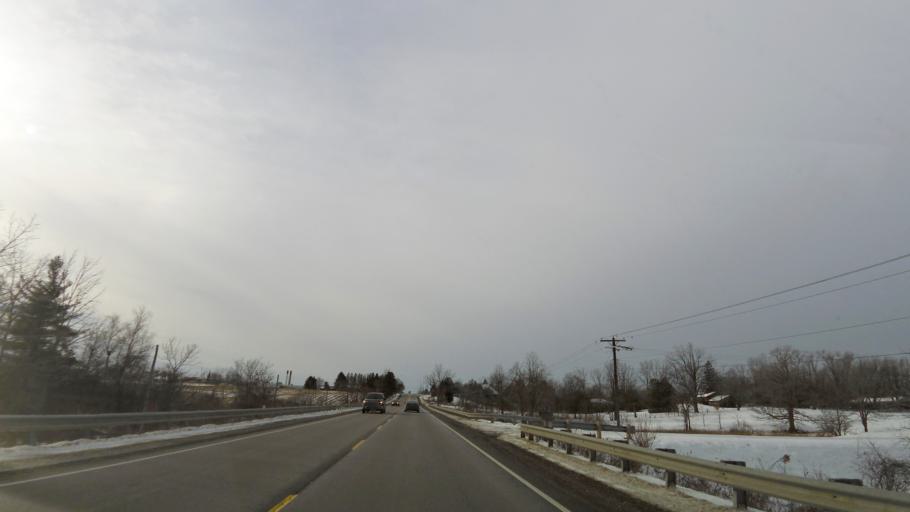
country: CA
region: Ontario
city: Ancaster
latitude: 43.2973
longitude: -79.9724
